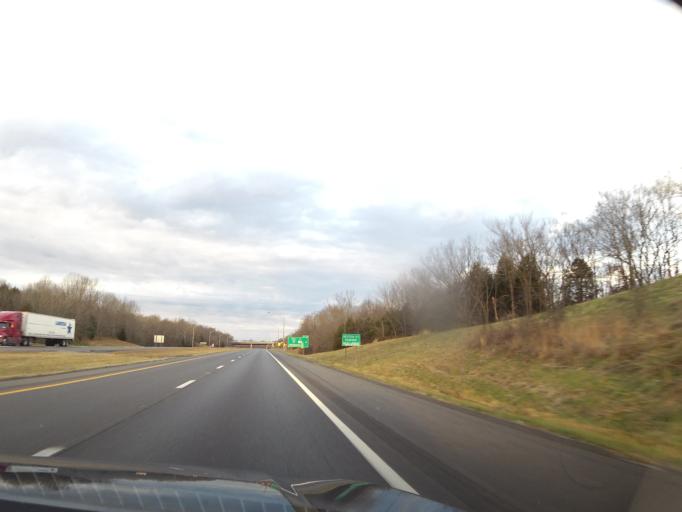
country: US
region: Kentucky
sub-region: Lyon County
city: Eddyville
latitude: 37.0692
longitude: -88.0775
